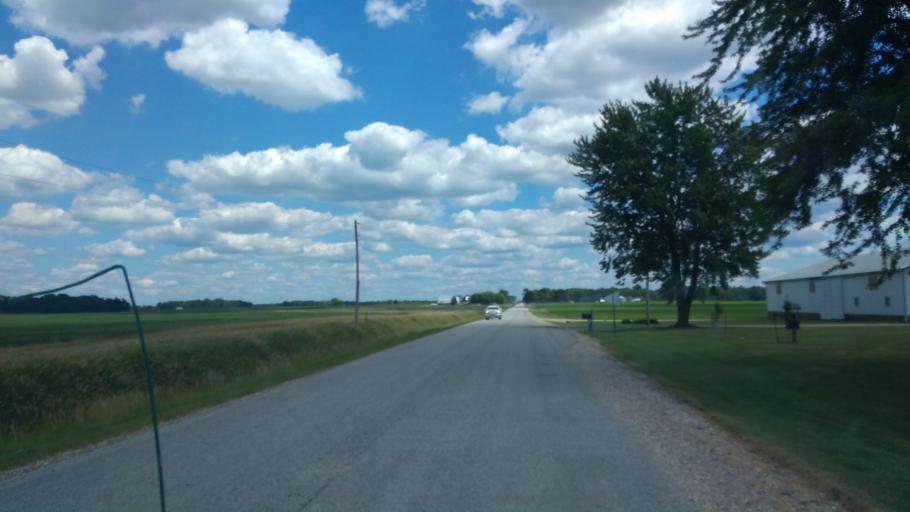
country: US
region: Indiana
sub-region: Adams County
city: Geneva
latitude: 40.5907
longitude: -85.0367
